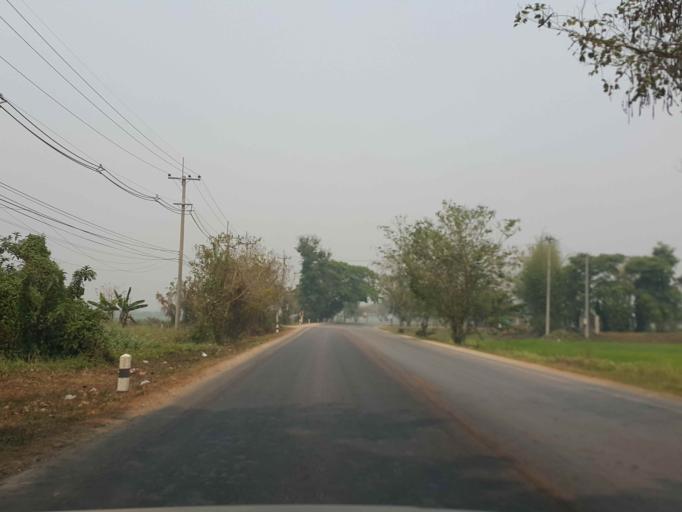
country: TH
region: Chiang Mai
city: Mae Taeng
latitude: 19.0602
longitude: 98.9585
